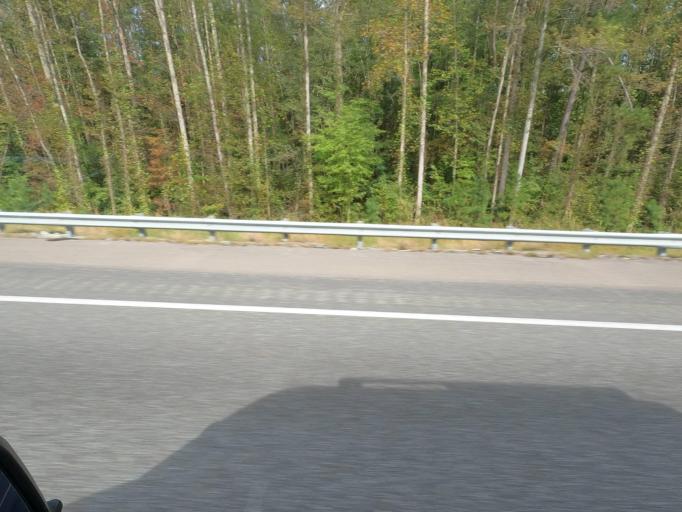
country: US
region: Tennessee
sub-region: Decatur County
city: Parsons
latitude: 35.8181
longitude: -88.2429
